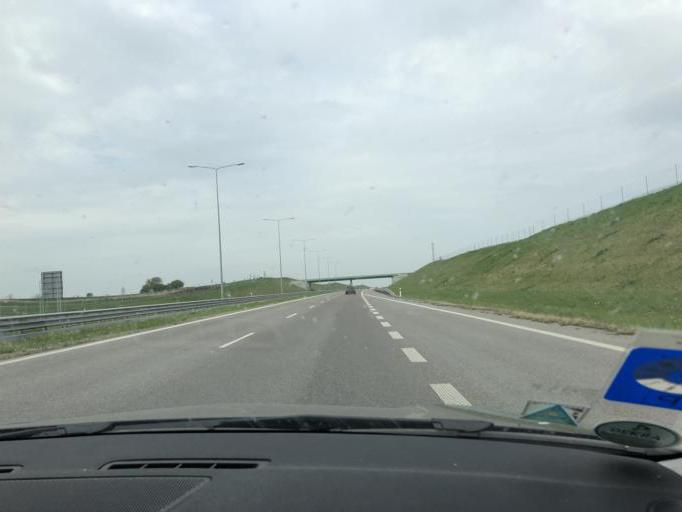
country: PL
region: Subcarpathian Voivodeship
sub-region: Powiat jaroslawski
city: Wierzbna
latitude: 49.9977
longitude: 22.6046
